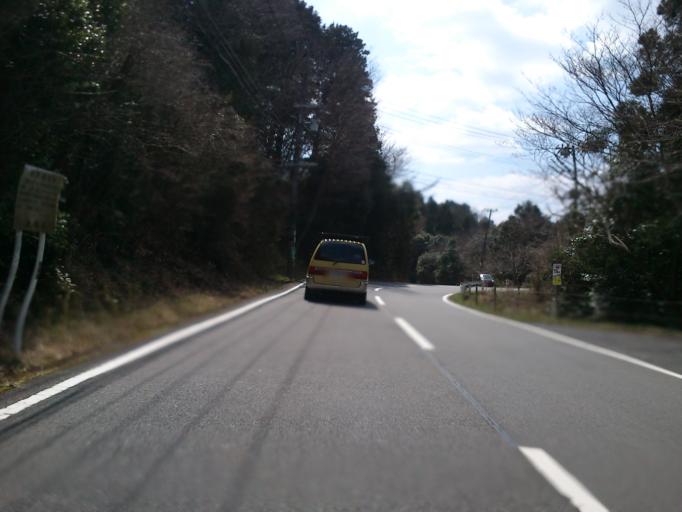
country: JP
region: Mie
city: Ueno-ebisumachi
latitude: 34.7459
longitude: 136.0230
